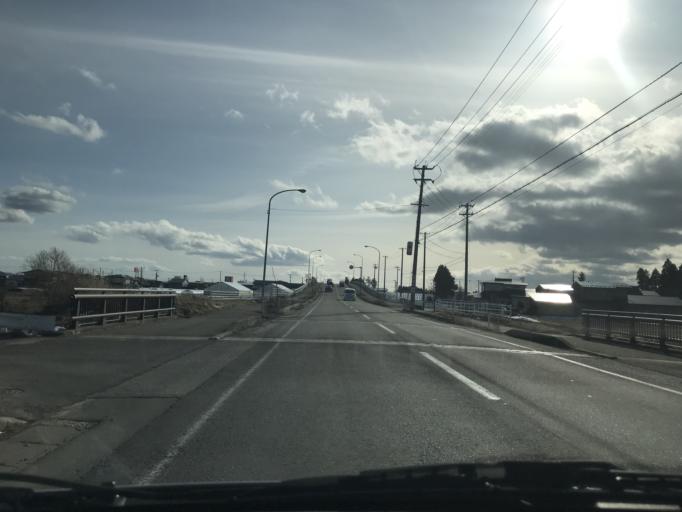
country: JP
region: Iwate
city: Kitakami
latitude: 39.2981
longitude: 141.0981
